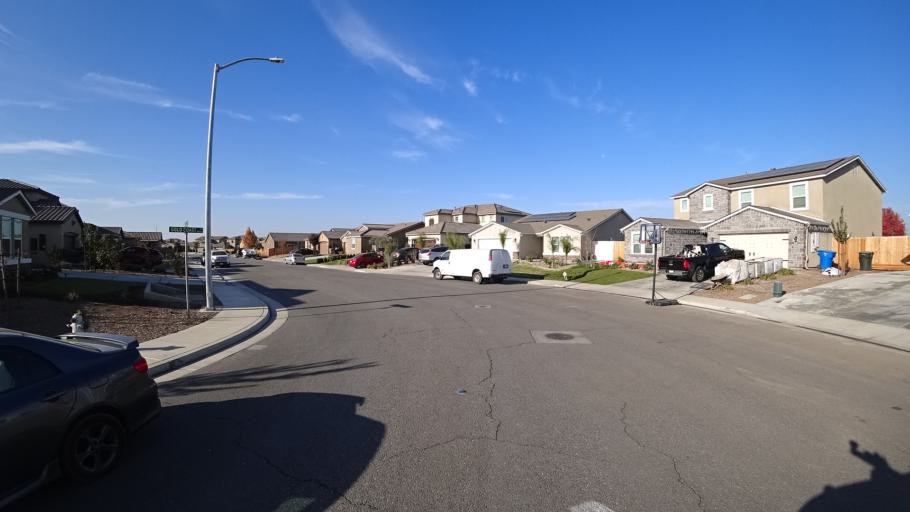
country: US
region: California
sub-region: Kern County
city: Greenfield
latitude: 35.2809
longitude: -119.0666
